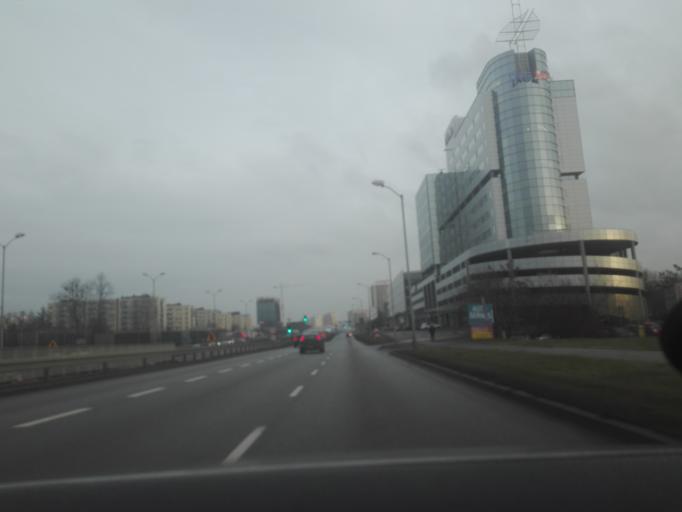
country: PL
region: Silesian Voivodeship
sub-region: Katowice
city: Katowice
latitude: 50.2664
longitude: 19.0138
